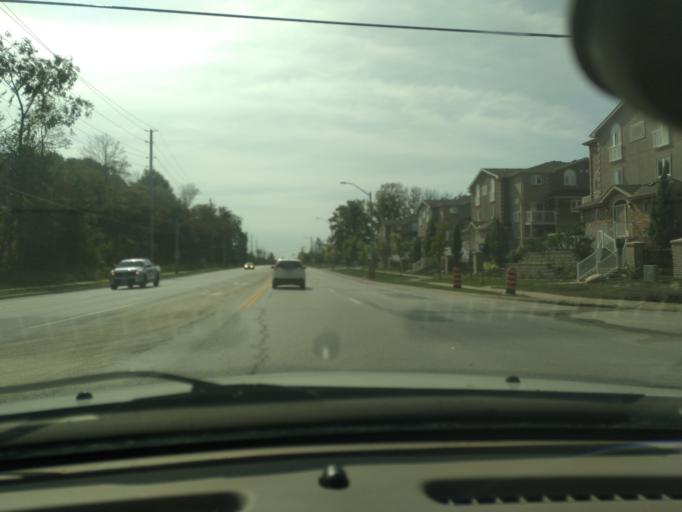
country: CA
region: Ontario
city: Barrie
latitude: 44.3449
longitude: -79.7020
